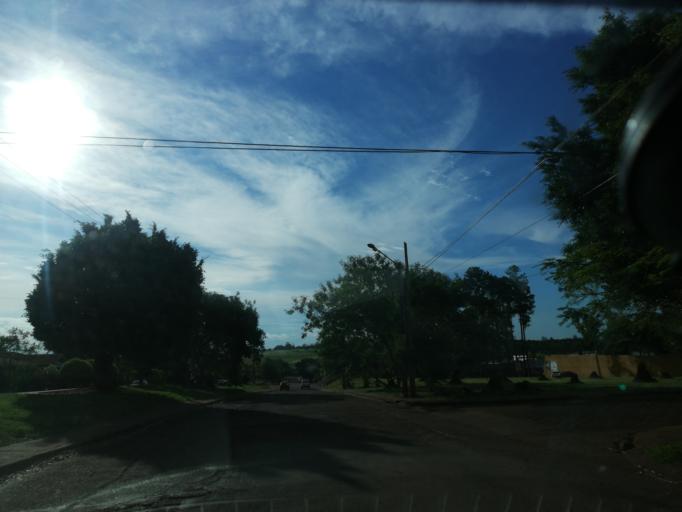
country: AR
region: Misiones
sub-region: Departamento de Capital
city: Posadas
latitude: -27.4149
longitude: -55.9548
